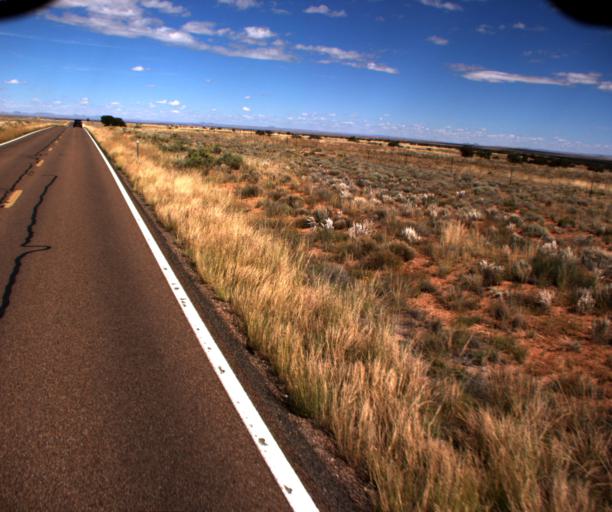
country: US
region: Arizona
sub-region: Navajo County
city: Holbrook
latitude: 34.7109
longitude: -110.2988
